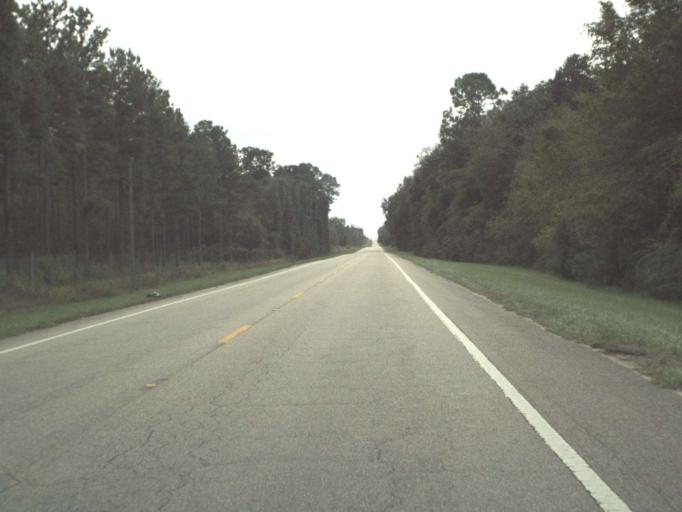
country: US
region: Florida
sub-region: Jackson County
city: Marianna
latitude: 30.6172
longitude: -85.1808
